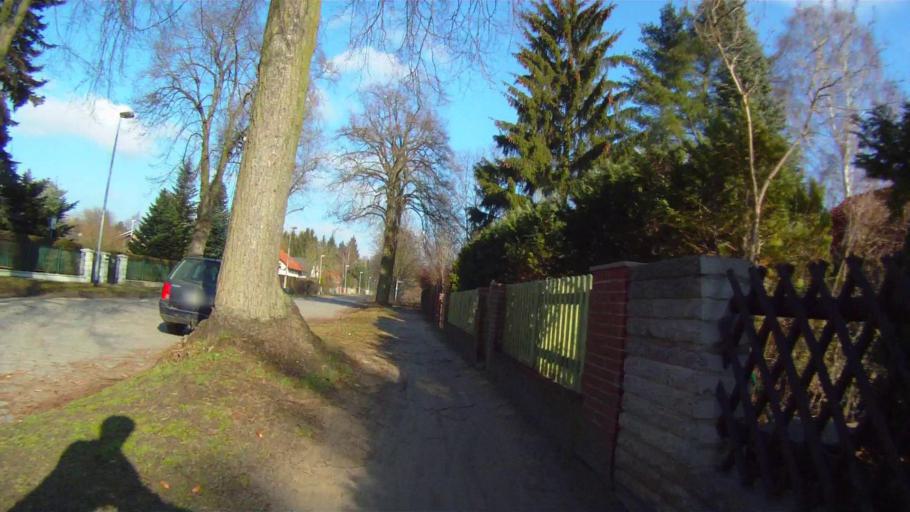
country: DE
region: Brandenburg
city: Schoneiche
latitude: 52.4695
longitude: 13.7157
